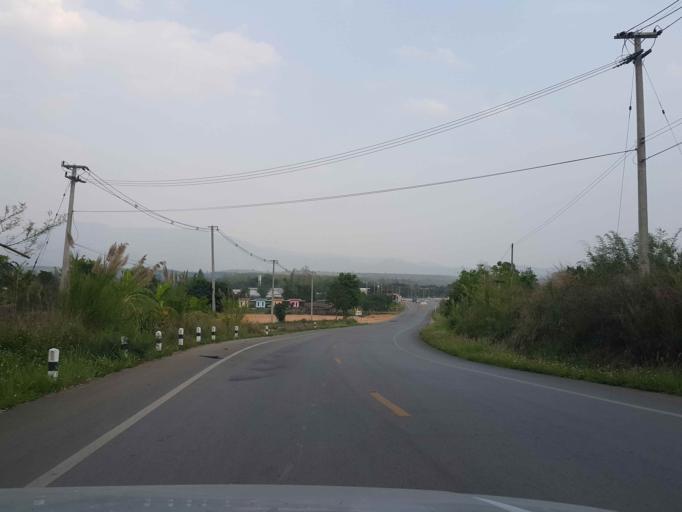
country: TH
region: Chiang Mai
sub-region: Amphoe Chiang Dao
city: Chiang Dao
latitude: 19.3532
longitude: 98.9571
